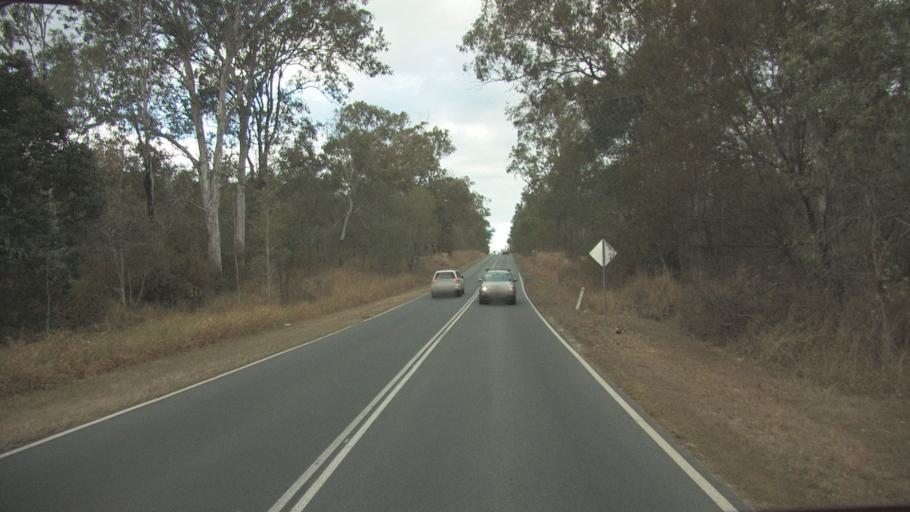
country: AU
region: Queensland
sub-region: Logan
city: Cedar Vale
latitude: -27.8869
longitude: 153.0805
